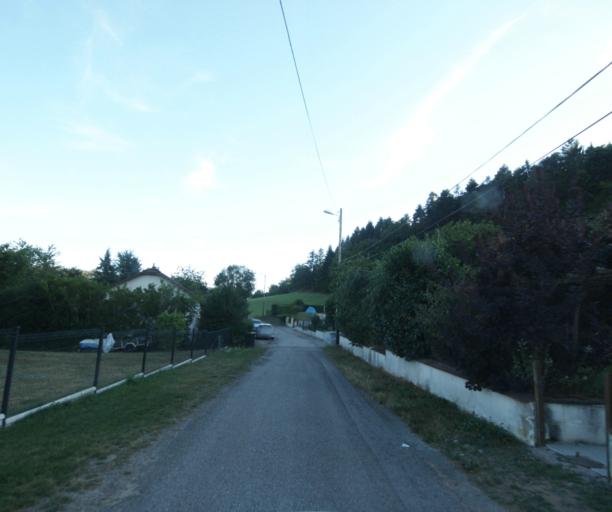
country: FR
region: Lorraine
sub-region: Departement des Vosges
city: Chantraine
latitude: 48.1437
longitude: 6.4493
